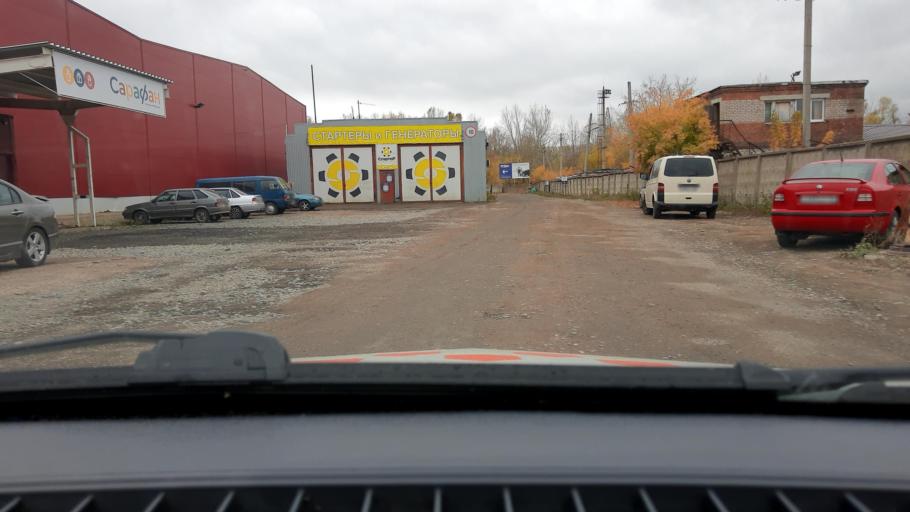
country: RU
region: Bashkortostan
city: Ufa
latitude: 54.7895
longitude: 56.0898
